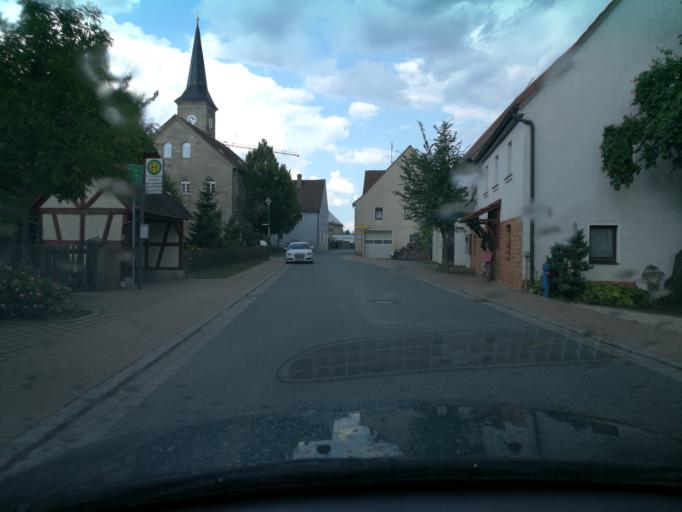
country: DE
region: Bavaria
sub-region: Regierungsbezirk Mittelfranken
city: Langenzenn
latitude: 49.4673
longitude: 10.7774
